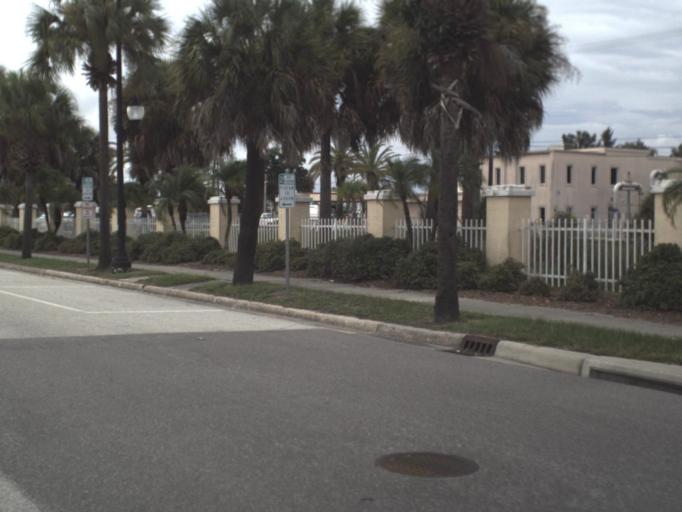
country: US
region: Florida
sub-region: Sarasota County
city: Venice
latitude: 27.0999
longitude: -82.4369
